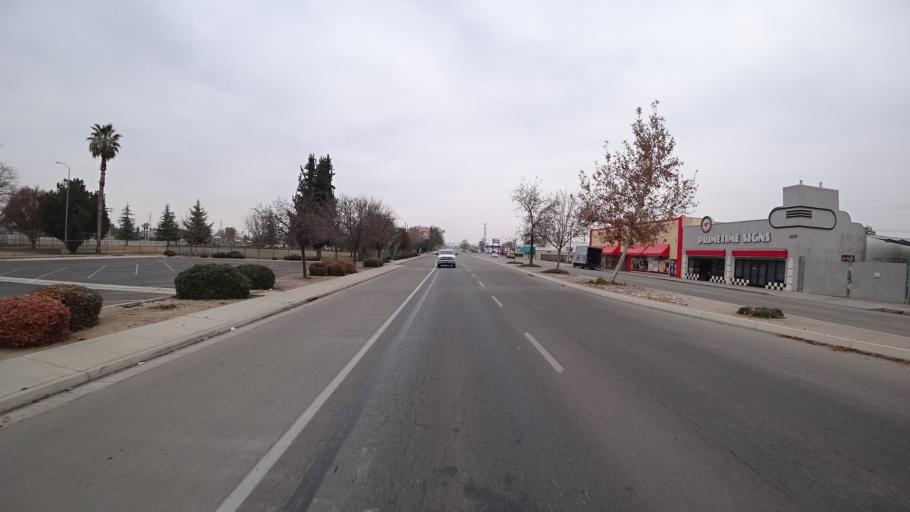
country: US
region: California
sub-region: Kern County
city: Bakersfield
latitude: 35.3949
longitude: -119.0188
